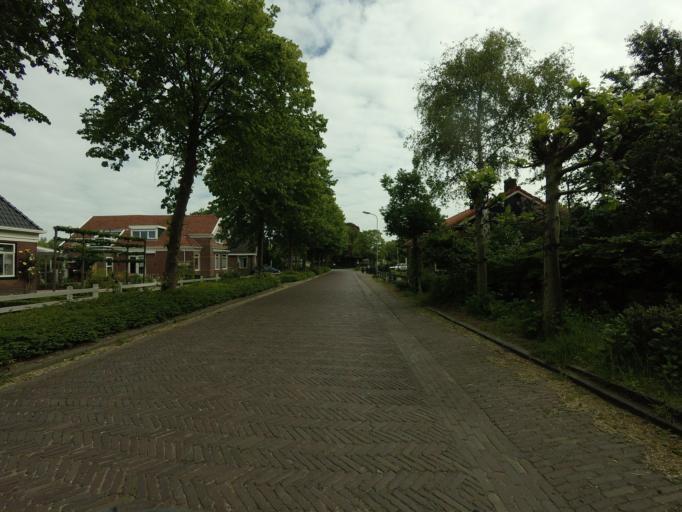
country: NL
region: North Holland
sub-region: Gemeente Medemblik
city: Opperdoes
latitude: 52.7068
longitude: 5.0986
